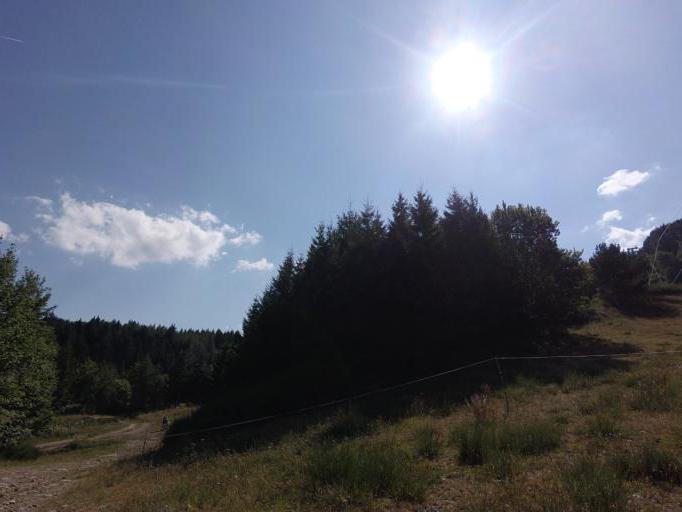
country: IT
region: Emilia-Romagna
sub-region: Provincia di Modena
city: Montecreto
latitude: 44.1979
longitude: 10.7303
